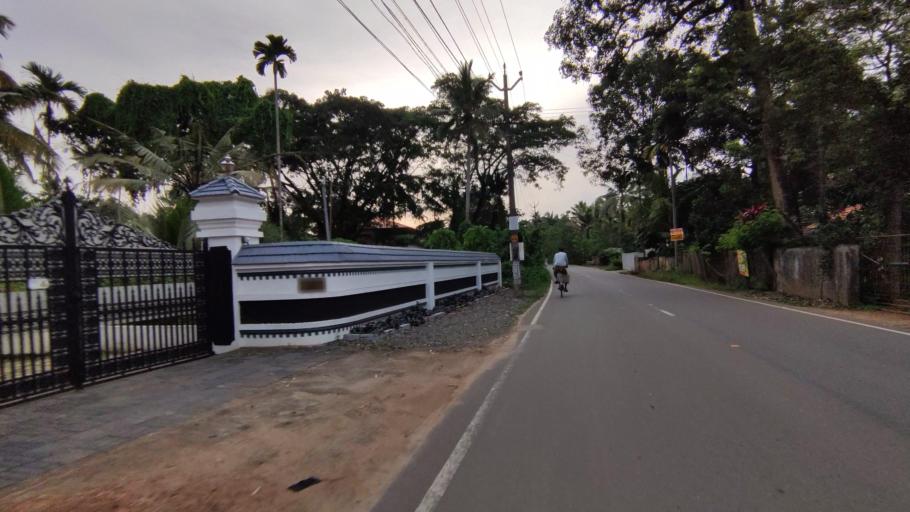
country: IN
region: Kerala
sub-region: Alappuzha
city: Shertallai
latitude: 9.6580
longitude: 76.3657
